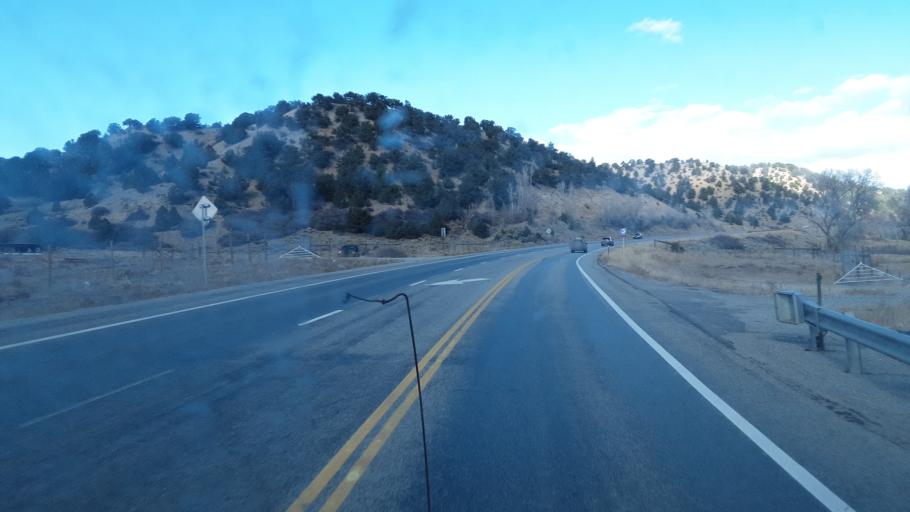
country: US
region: Colorado
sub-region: Chaffee County
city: Buena Vista
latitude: 38.7821
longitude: -106.1130
